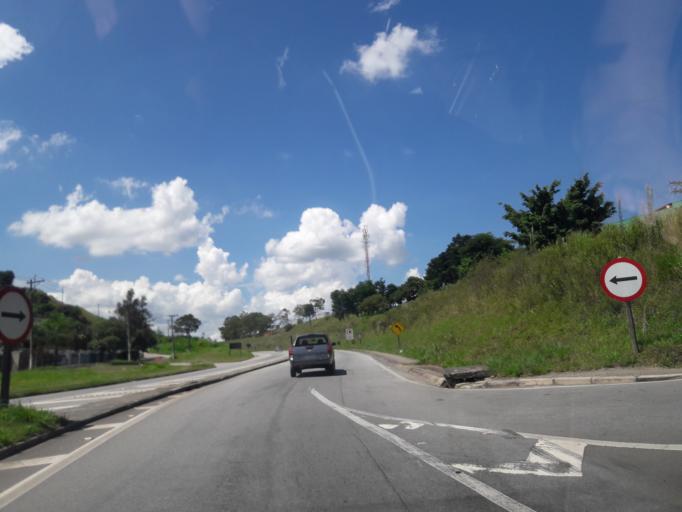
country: BR
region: Sao Paulo
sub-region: Cajamar
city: Cajamar
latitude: -23.3402
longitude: -46.8265
